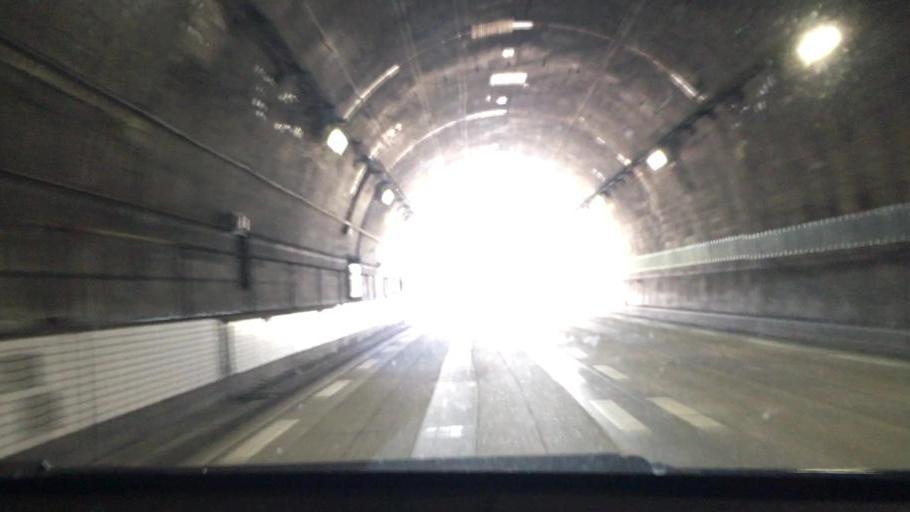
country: JP
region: Yamaguchi
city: Hofu
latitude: 34.0564
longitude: 131.6182
